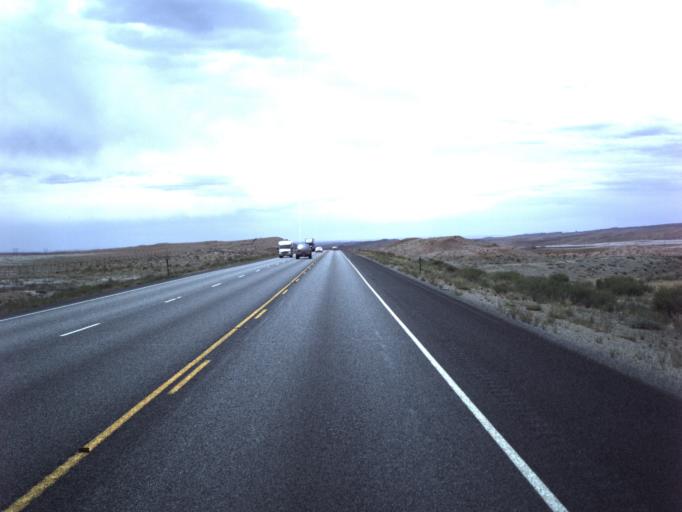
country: US
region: Utah
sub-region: Carbon County
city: East Carbon City
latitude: 39.1509
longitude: -110.3376
